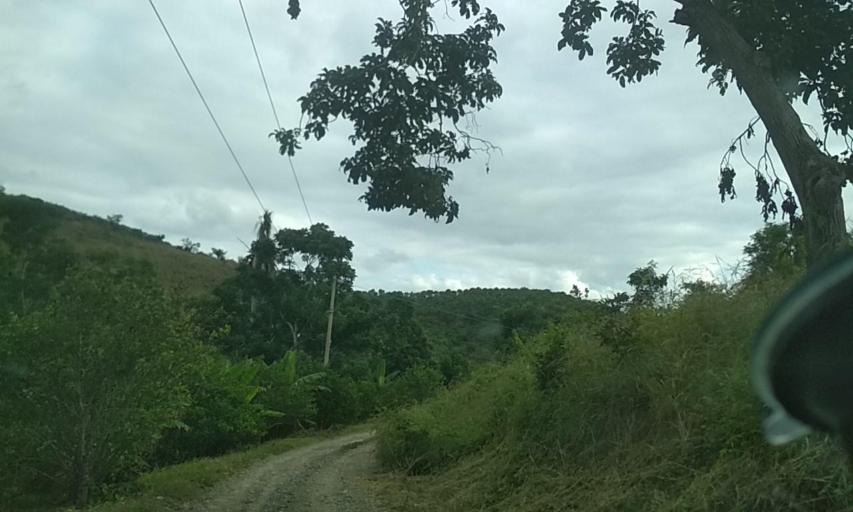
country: MX
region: Veracruz
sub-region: Papantla
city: Polutla
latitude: 20.5822
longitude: -97.2775
